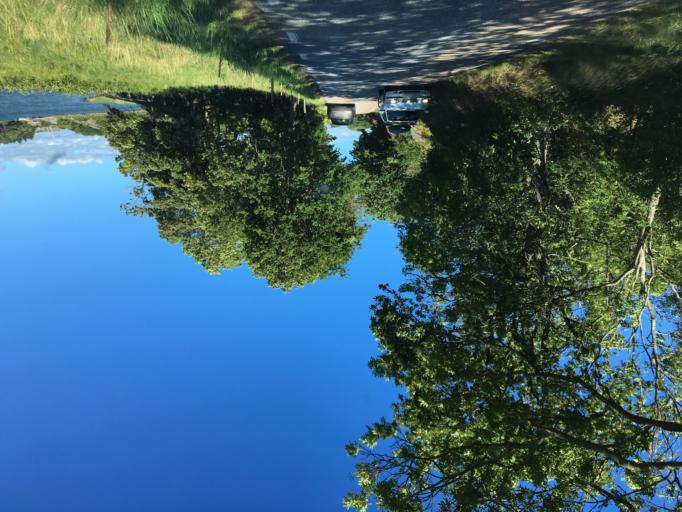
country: SE
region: Vaestra Goetaland
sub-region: Sotenas Kommun
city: Hunnebostrand
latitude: 58.4226
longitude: 11.2656
